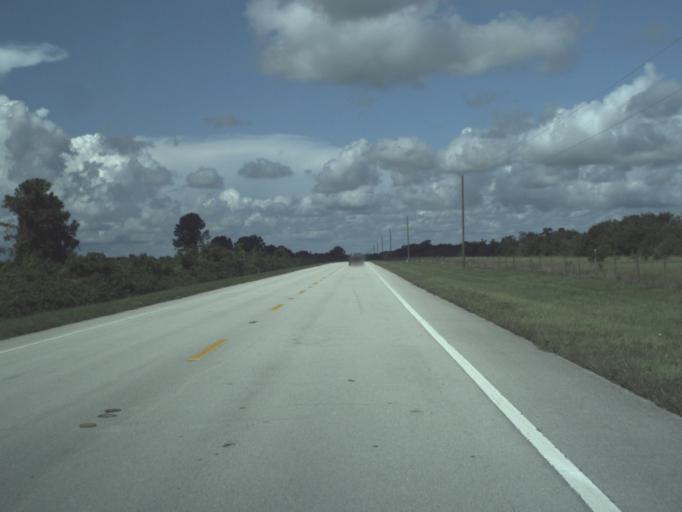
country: US
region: Florida
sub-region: Highlands County
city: Lake Placid
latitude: 27.3852
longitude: -81.1345
